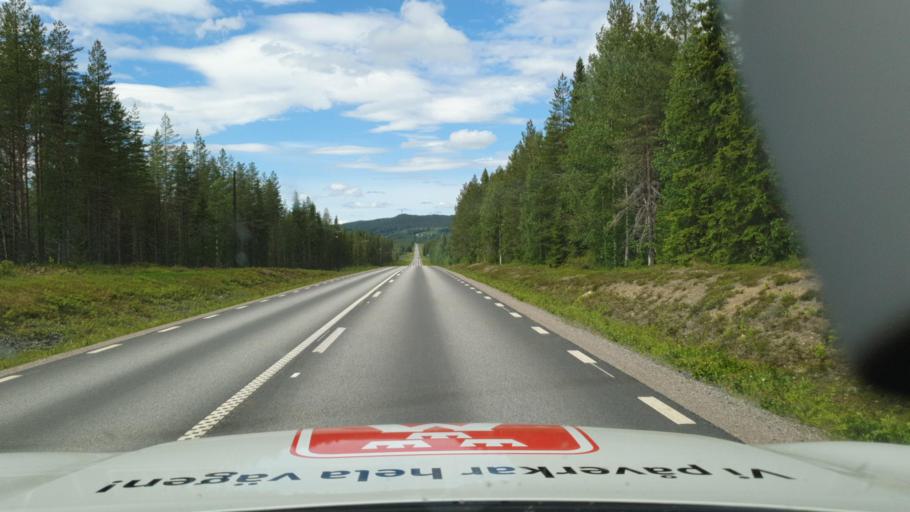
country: SE
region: Vaesterbotten
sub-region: Norsjo Kommun
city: Norsjoe
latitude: 65.2461
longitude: 19.7006
